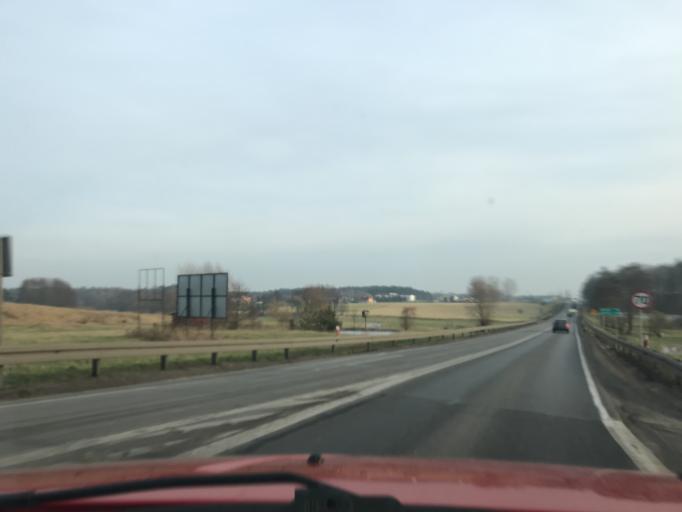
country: PL
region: Greater Poland Voivodeship
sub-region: Powiat jarocinski
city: Kotlin
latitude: 51.9371
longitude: 17.6068
